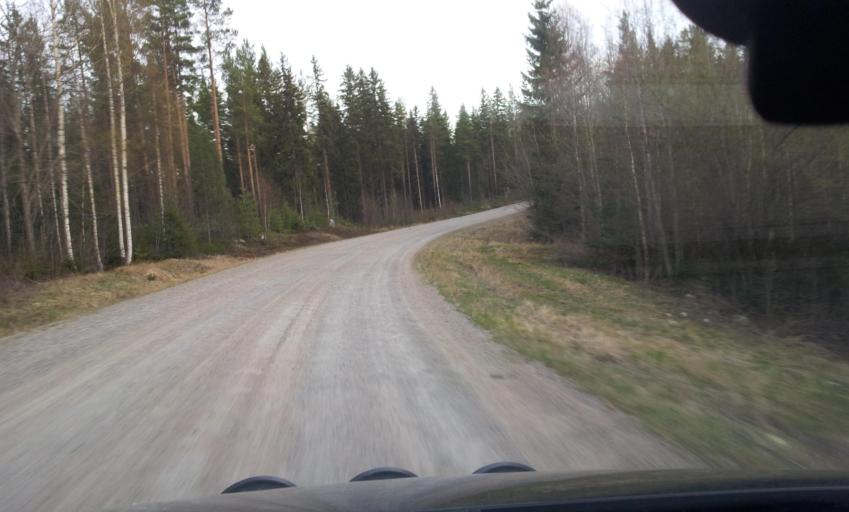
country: SE
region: Gaevleborg
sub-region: Ljusdals Kommun
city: Farila
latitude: 62.0073
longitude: 15.8383
